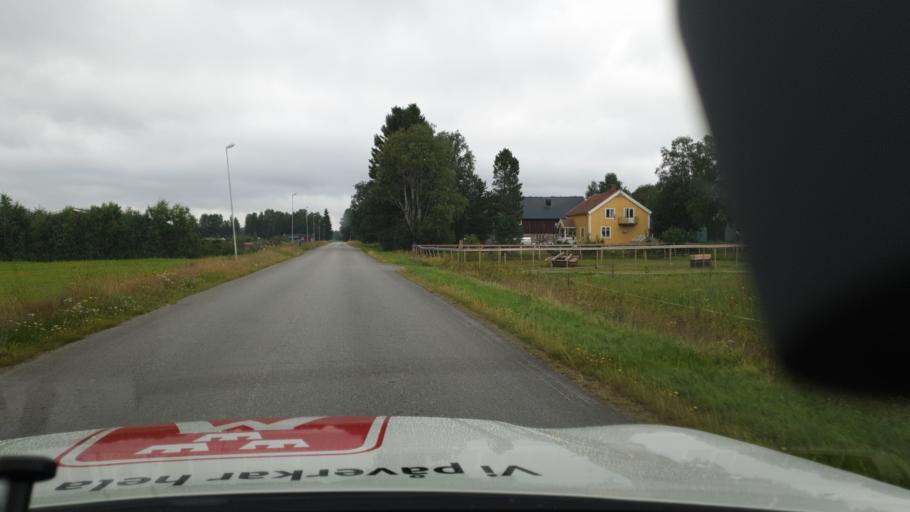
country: SE
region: Vaesterbotten
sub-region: Vannas Kommun
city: Vannasby
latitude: 63.9517
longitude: 19.8679
